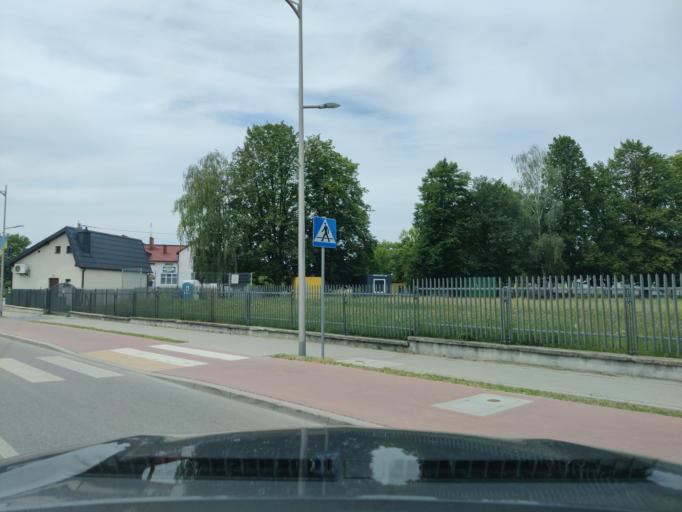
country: PL
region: Masovian Voivodeship
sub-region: Powiat wyszkowski
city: Wyszkow
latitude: 52.6009
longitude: 21.4568
